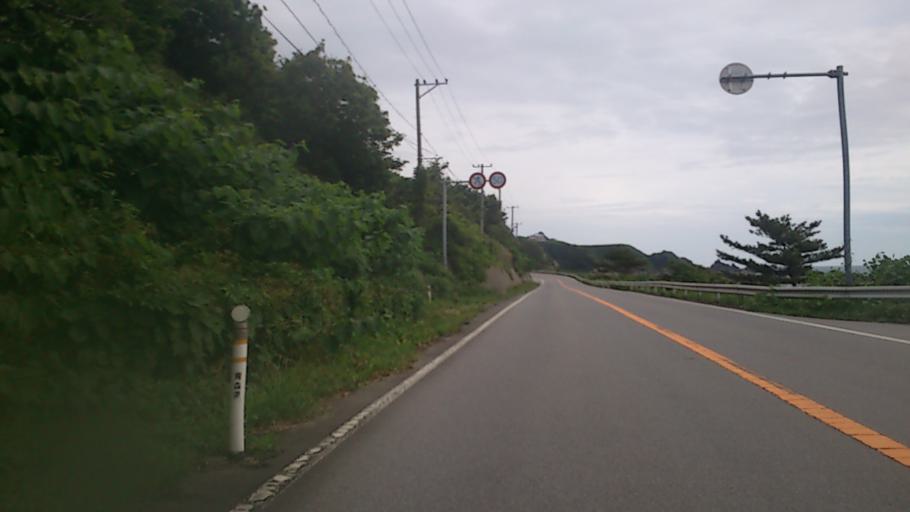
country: JP
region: Akita
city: Noshiromachi
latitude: 40.4420
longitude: 139.9405
